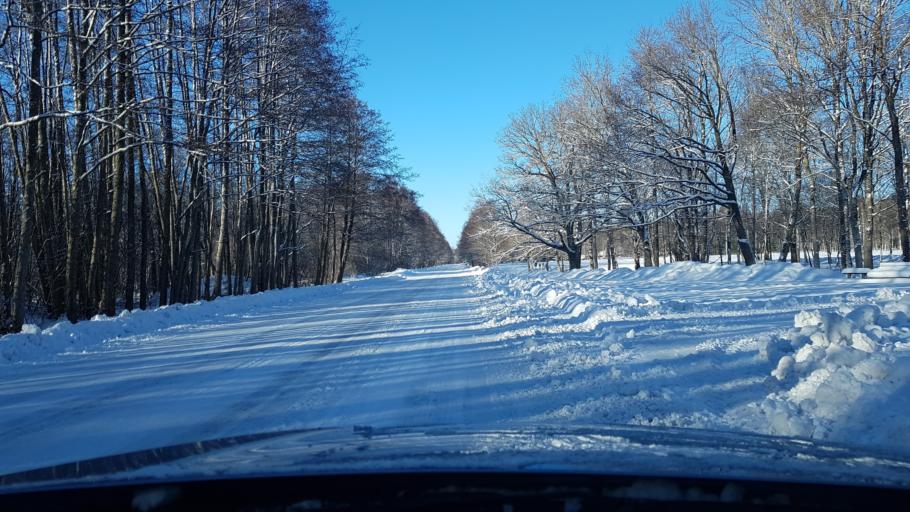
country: EE
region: Hiiumaa
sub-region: Kaerdla linn
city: Kardla
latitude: 58.8250
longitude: 22.7465
